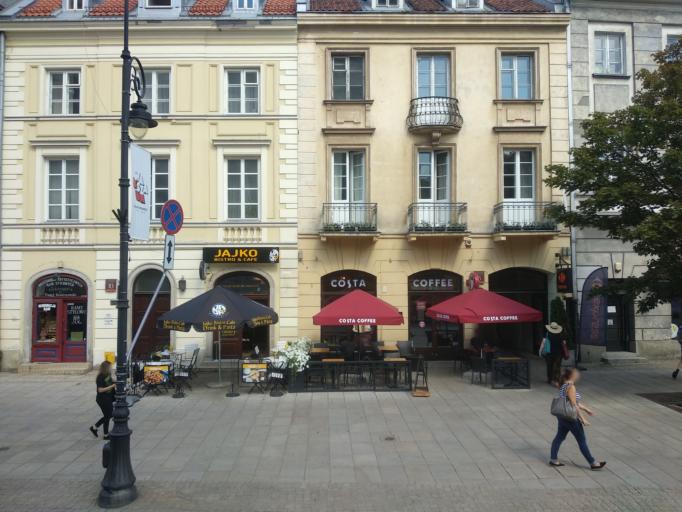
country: PL
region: Masovian Voivodeship
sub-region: Warszawa
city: Srodmiescie
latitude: 52.2388
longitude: 21.0175
